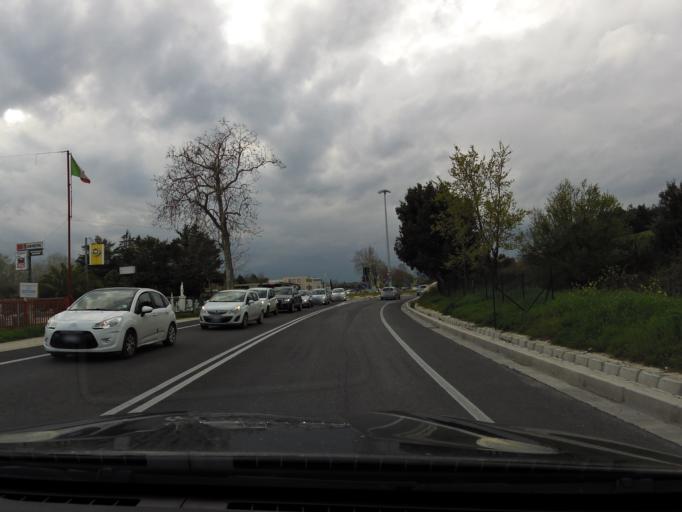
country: IT
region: The Marches
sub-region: Provincia di Macerata
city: Porto Recanati
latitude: 43.4354
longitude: 13.6466
